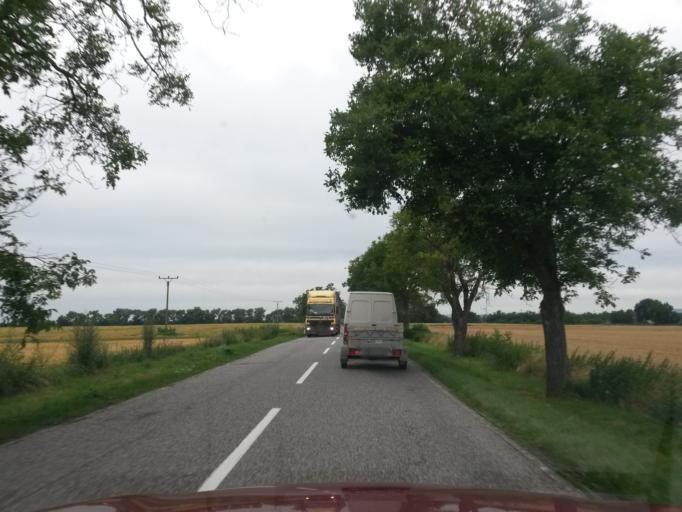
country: SK
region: Nitriansky
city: Levice
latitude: 48.1389
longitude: 18.5875
